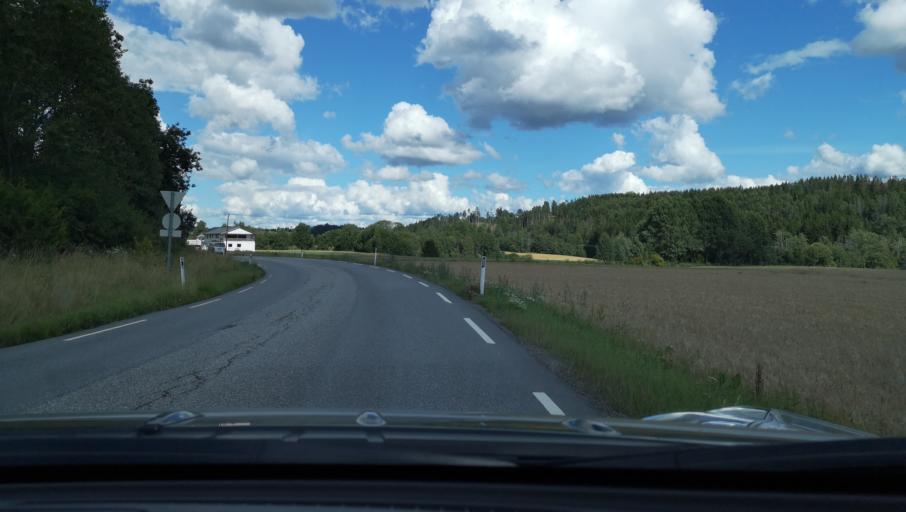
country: NO
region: Ostfold
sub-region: Hobol
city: Elvestad
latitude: 59.6305
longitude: 10.9575
